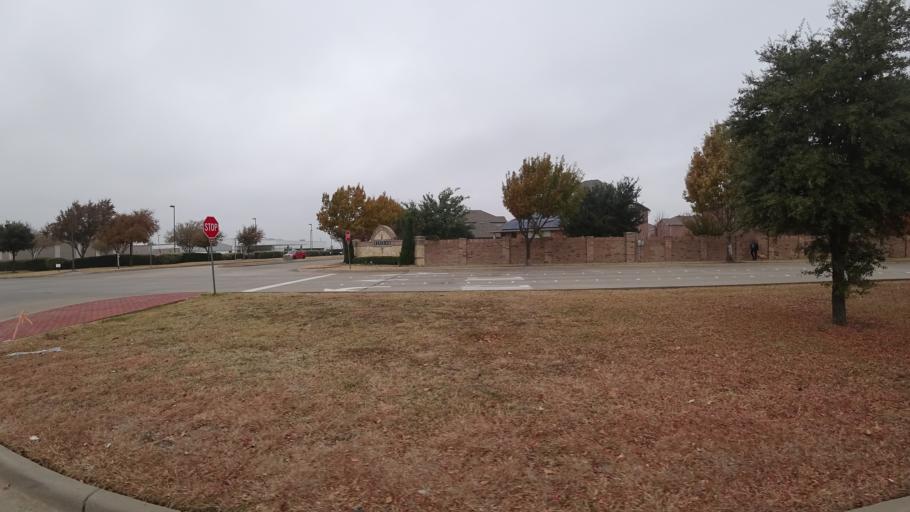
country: US
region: Texas
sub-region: Denton County
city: The Colony
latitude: 33.0642
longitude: -96.9015
